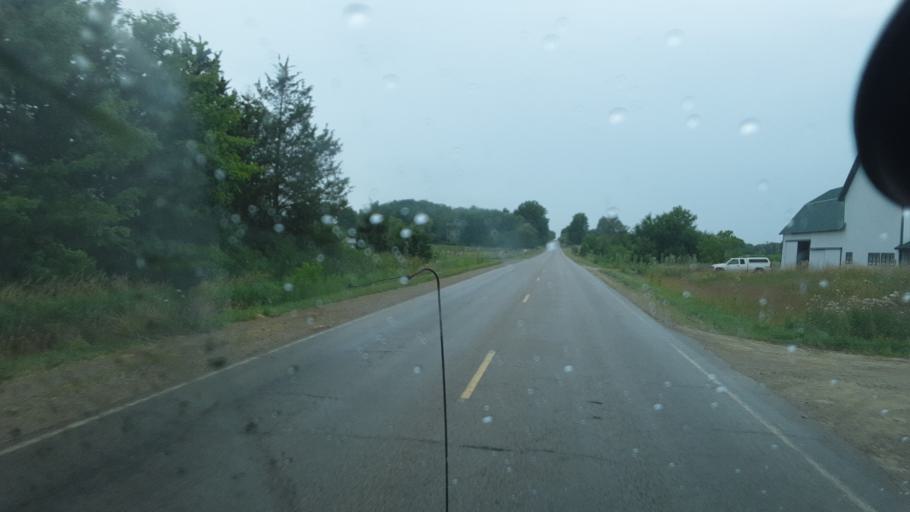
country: US
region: Michigan
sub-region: Hillsdale County
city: Reading
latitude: 41.7080
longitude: -84.7628
